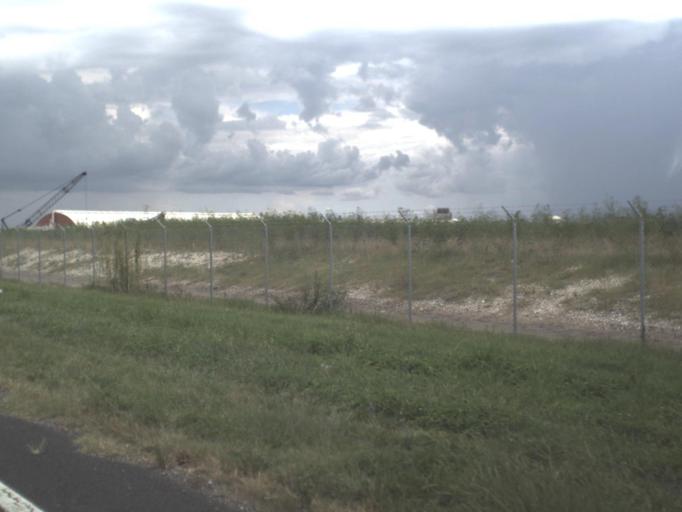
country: US
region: Florida
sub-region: Hillsborough County
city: Tampa
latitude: 27.9275
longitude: -82.4237
